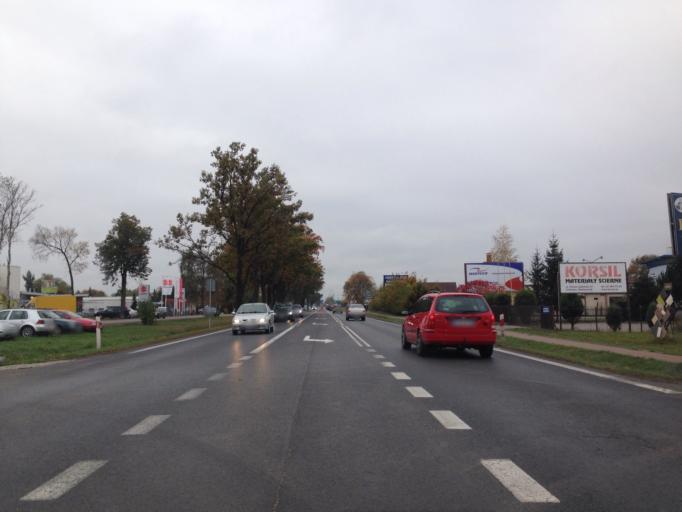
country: PL
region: Kujawsko-Pomorskie
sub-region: Powiat bydgoski
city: Osielsko
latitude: 53.1786
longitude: 18.0604
